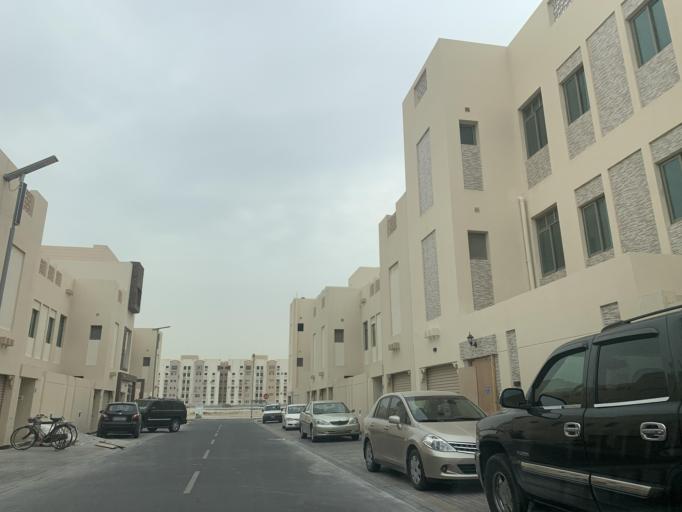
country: BH
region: Northern
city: Madinat `Isa
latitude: 26.1704
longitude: 50.5153
